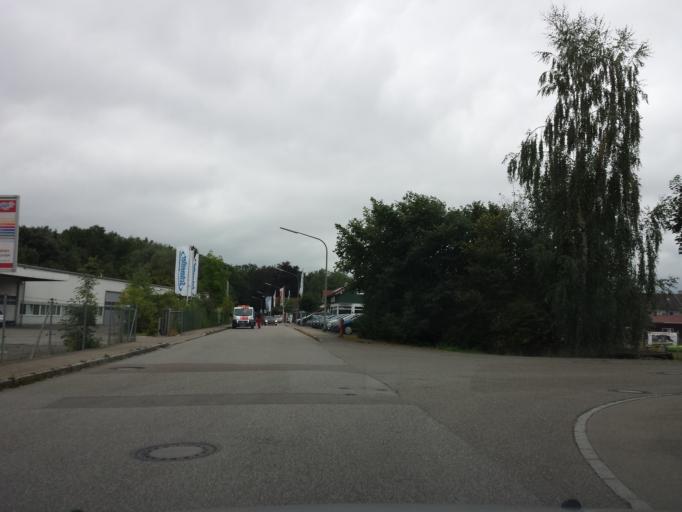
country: DE
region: Bavaria
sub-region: Swabia
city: Guenzburg
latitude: 48.4697
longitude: 10.2687
